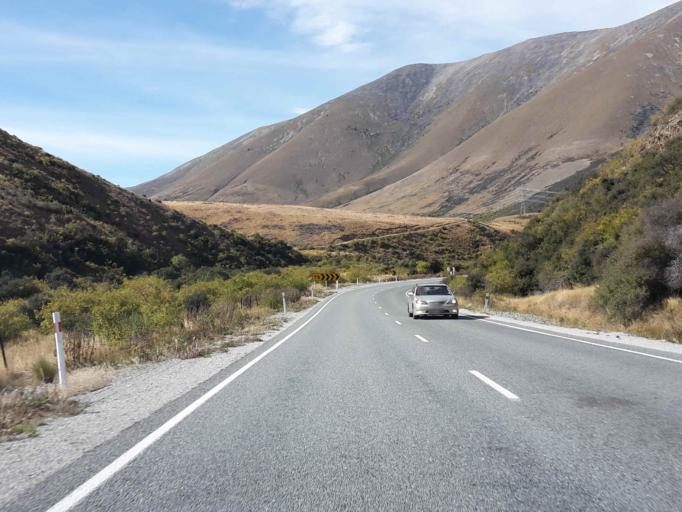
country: NZ
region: Otago
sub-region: Queenstown-Lakes District
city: Wanaka
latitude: -44.5599
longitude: 169.6767
